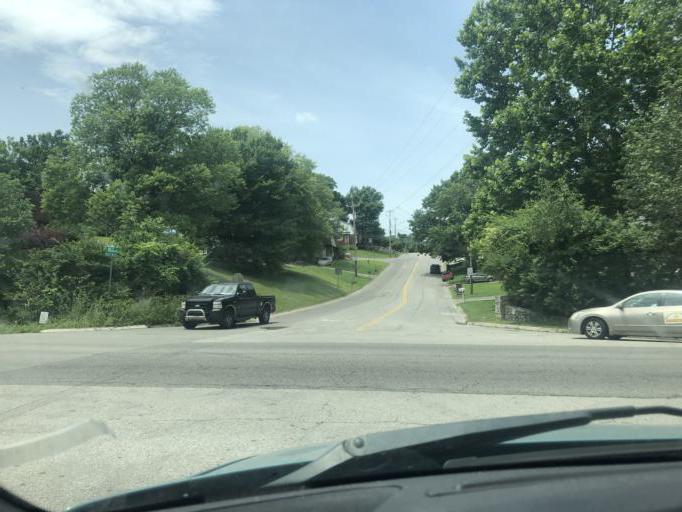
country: US
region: Tennessee
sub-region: Davidson County
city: Lakewood
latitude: 36.1275
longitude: -86.6294
